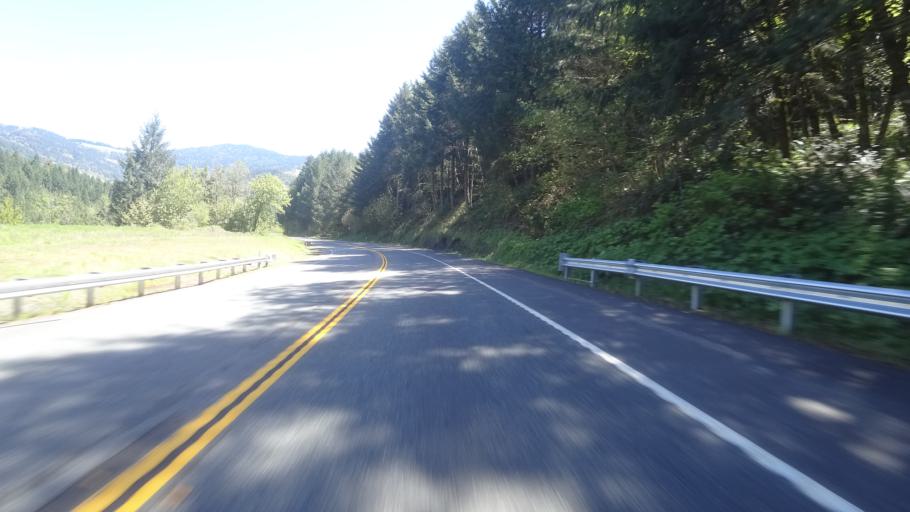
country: US
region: California
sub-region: Humboldt County
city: Blue Lake
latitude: 40.9045
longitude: -123.8272
